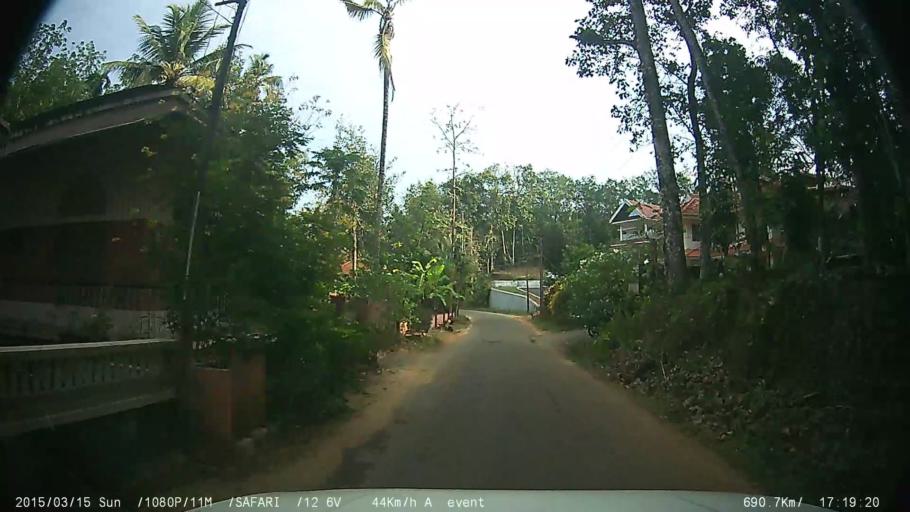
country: IN
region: Kerala
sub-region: Kottayam
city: Palackattumala
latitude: 9.8504
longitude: 76.7002
